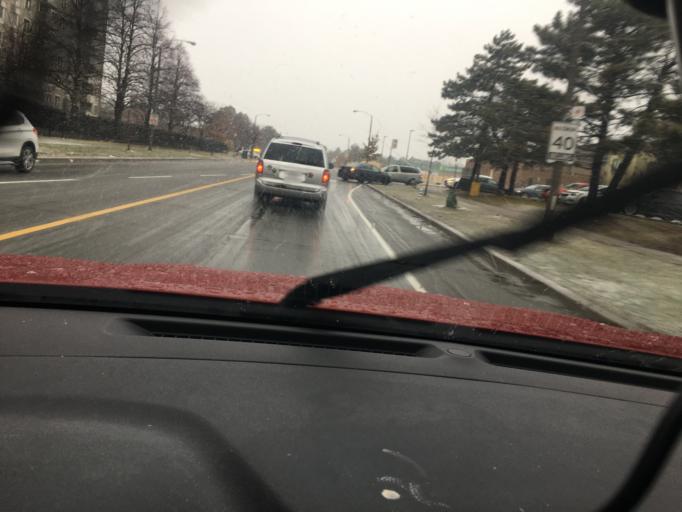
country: CA
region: Ontario
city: Scarborough
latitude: 43.8076
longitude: -79.2705
